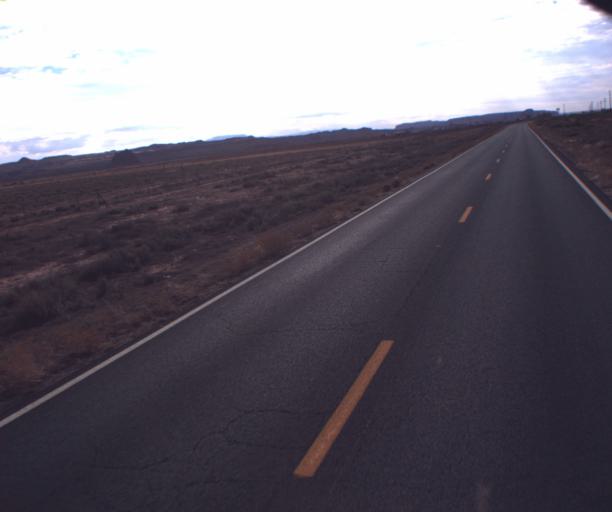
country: US
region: Arizona
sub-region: Apache County
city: Many Farms
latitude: 36.7417
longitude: -109.6375
